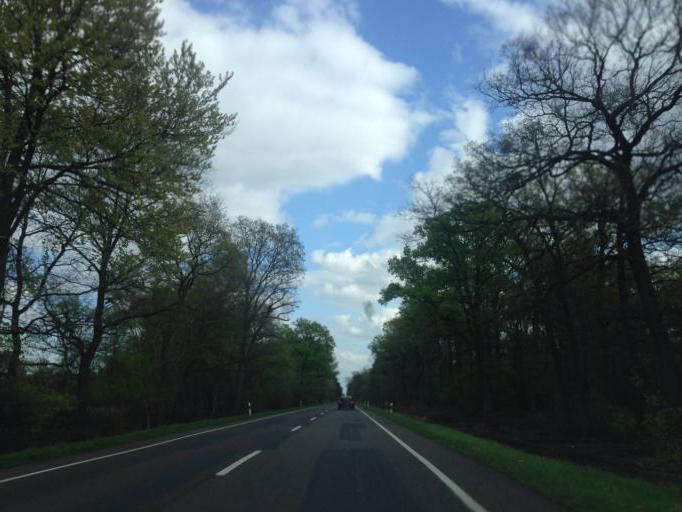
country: DE
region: Lower Saxony
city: Meinersen
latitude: 52.4679
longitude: 10.2837
